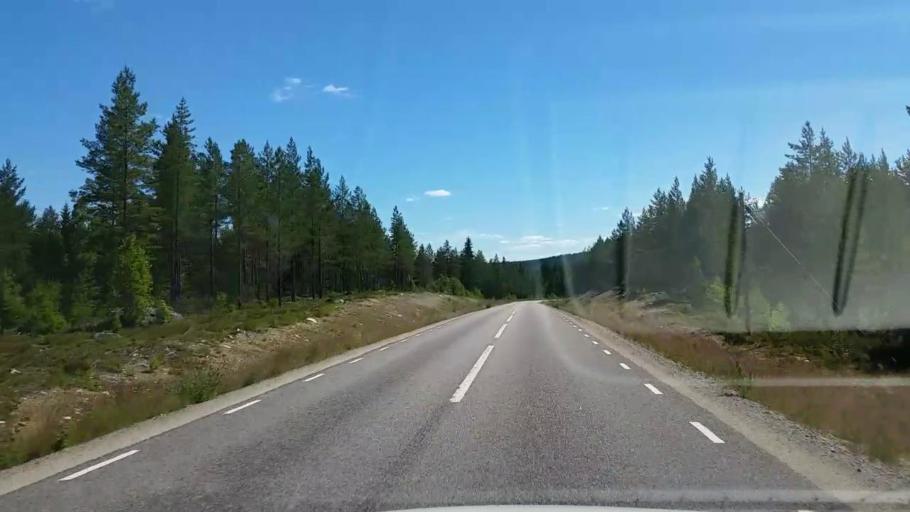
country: SE
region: Gaevleborg
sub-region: Ovanakers Kommun
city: Edsbyn
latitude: 61.4348
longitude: 15.7184
